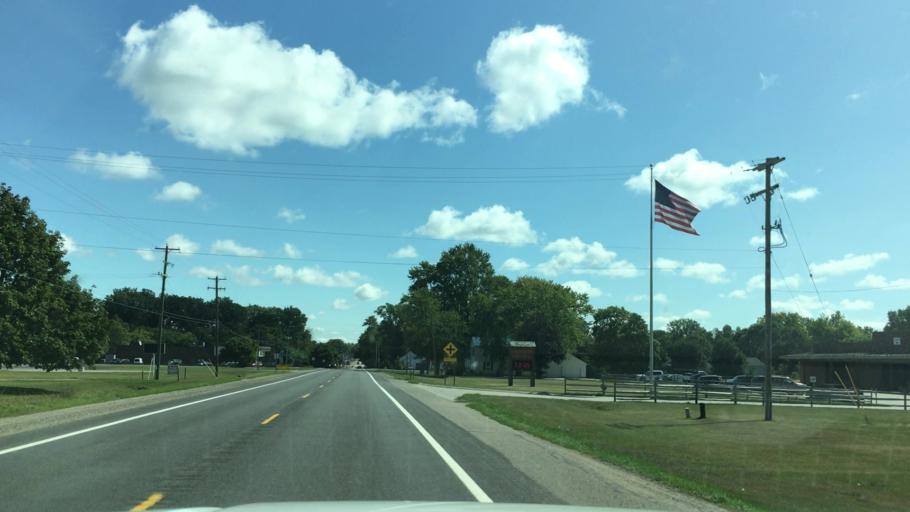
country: US
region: Michigan
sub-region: Montcalm County
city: Carson City
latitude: 43.1772
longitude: -84.8641
